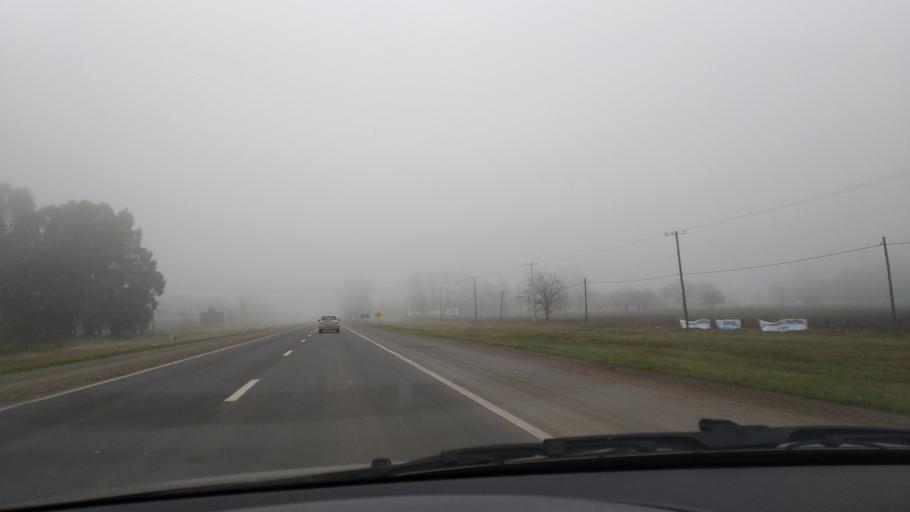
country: AR
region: Buenos Aires
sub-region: Partido de Azul
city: Azul
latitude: -36.8088
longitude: -59.8604
